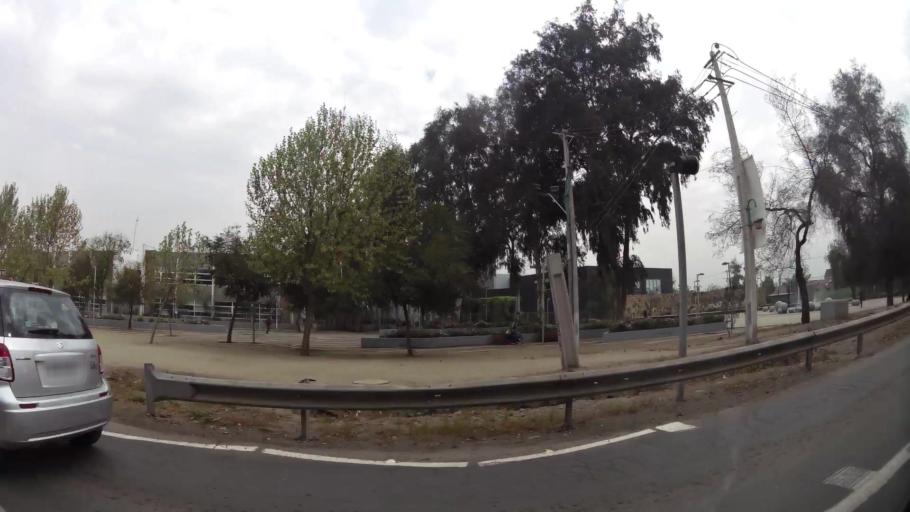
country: CL
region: Santiago Metropolitan
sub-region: Provincia de Chacabuco
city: Chicureo Abajo
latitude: -33.2048
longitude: -70.6832
